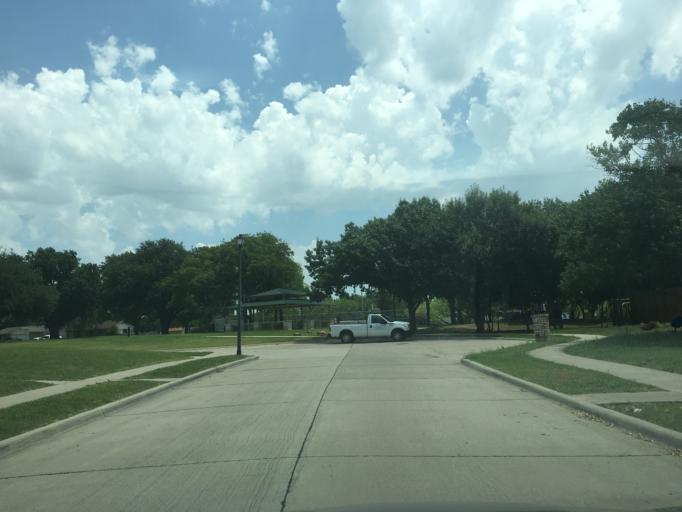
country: US
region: Texas
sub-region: Dallas County
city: Carrollton
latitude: 32.9496
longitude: -96.8789
